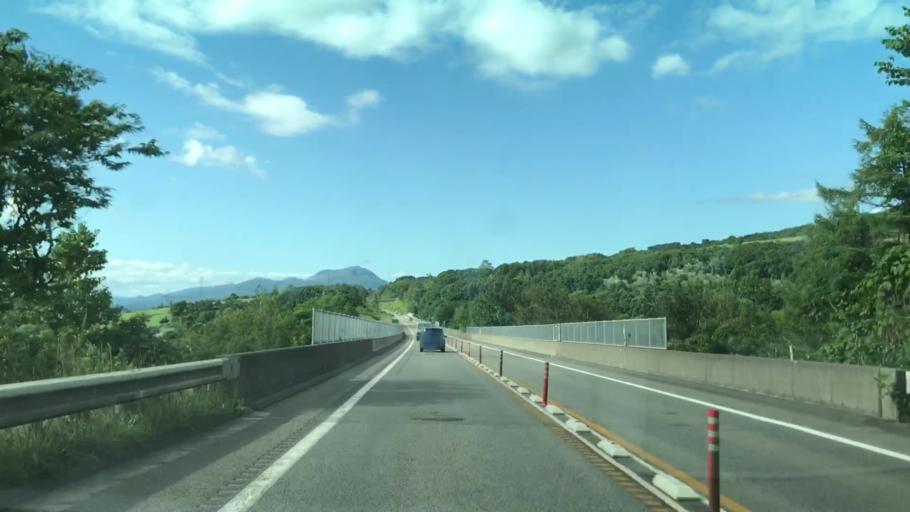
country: JP
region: Hokkaido
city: Date
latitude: 42.4314
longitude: 140.9246
